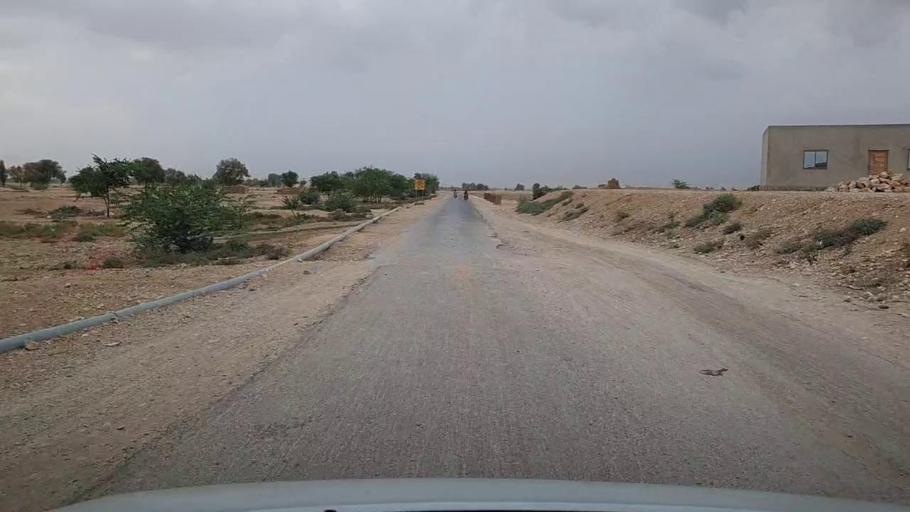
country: PK
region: Sindh
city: Sehwan
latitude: 26.3337
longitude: 67.7238
